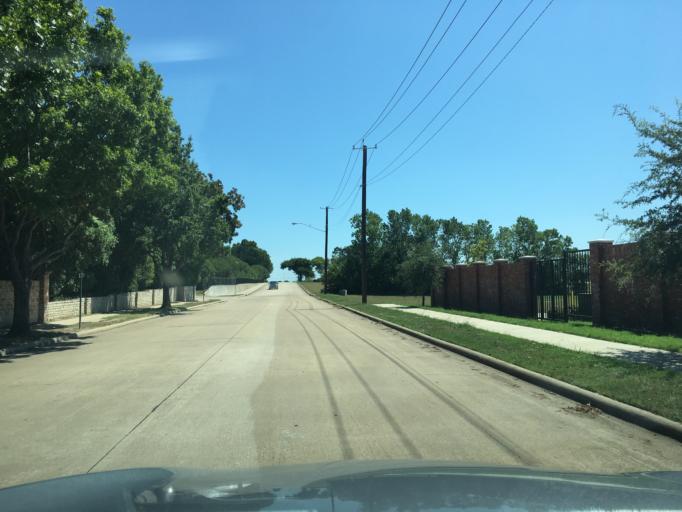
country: US
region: Texas
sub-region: Dallas County
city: Sachse
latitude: 32.9616
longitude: -96.6332
